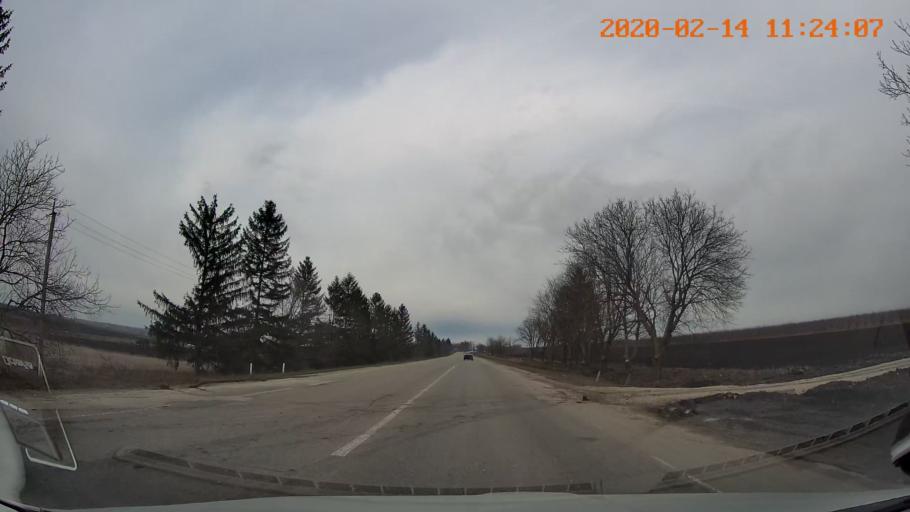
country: MD
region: Briceni
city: Briceni
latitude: 48.3336
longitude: 27.1191
